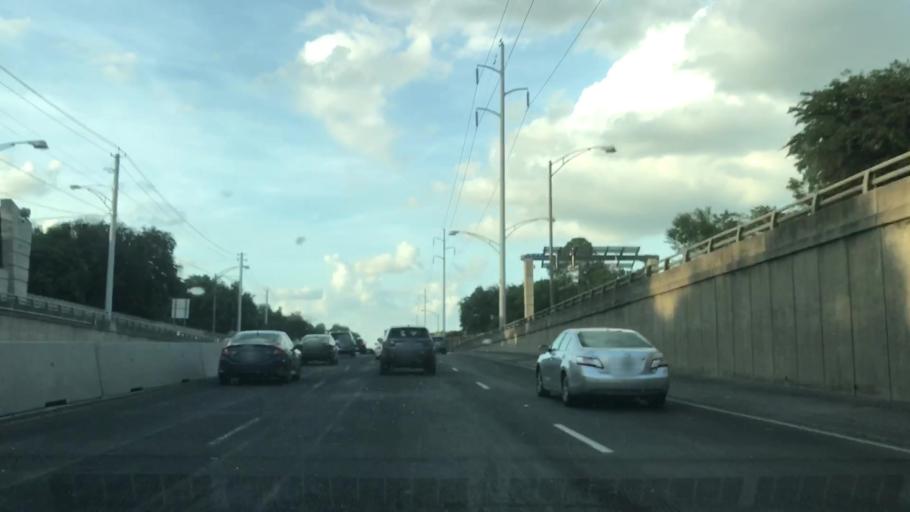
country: US
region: Texas
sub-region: Dallas County
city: University Park
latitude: 32.8374
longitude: -96.8148
